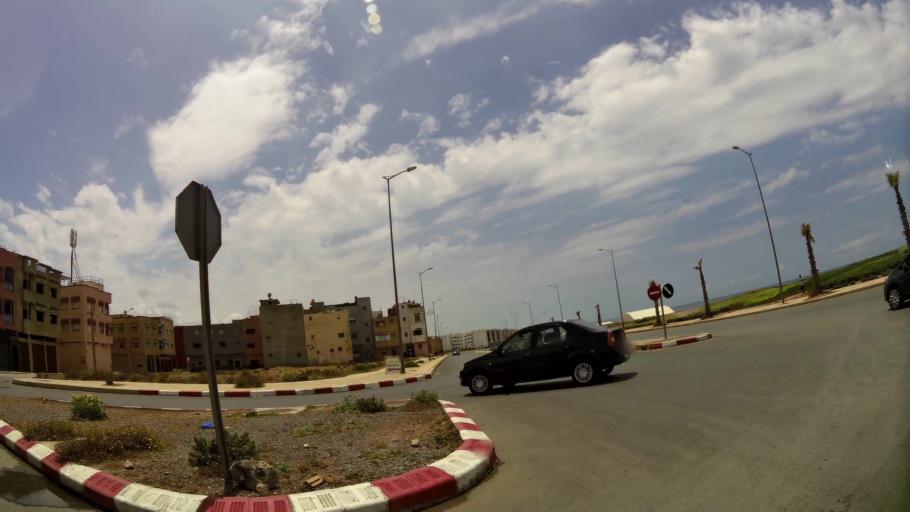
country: MA
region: Rabat-Sale-Zemmour-Zaer
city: Sale
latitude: 34.0640
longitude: -6.8088
